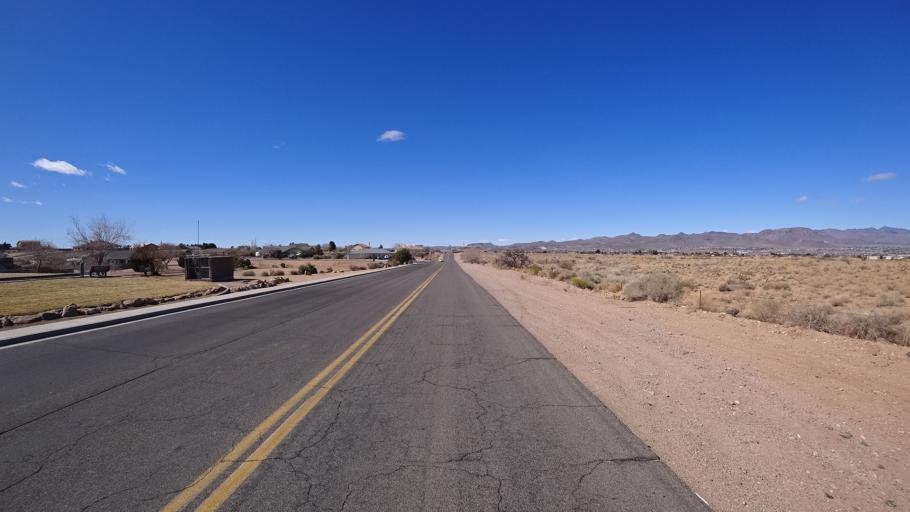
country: US
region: Arizona
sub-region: Mohave County
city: Kingman
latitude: 35.1958
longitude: -113.9884
